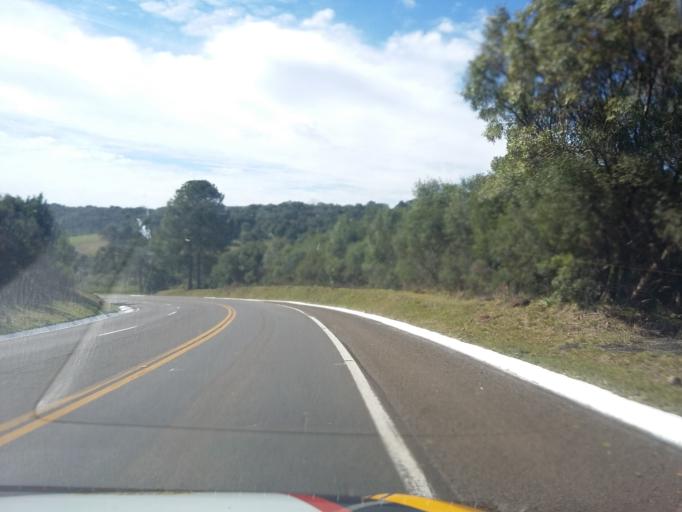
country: BR
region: Rio Grande do Sul
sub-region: Vacaria
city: Vacaria
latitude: -28.5764
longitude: -51.0146
